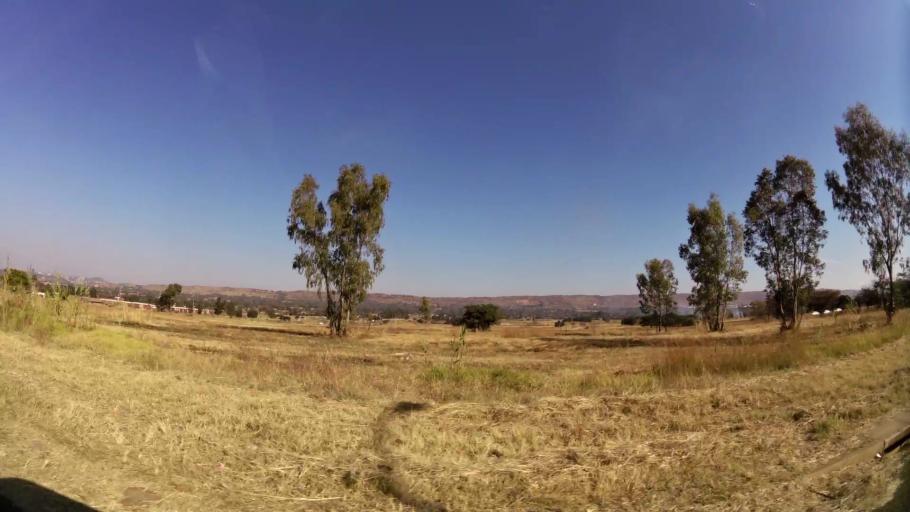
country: ZA
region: Gauteng
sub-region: City of Tshwane Metropolitan Municipality
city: Pretoria
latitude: -25.6967
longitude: 28.1383
